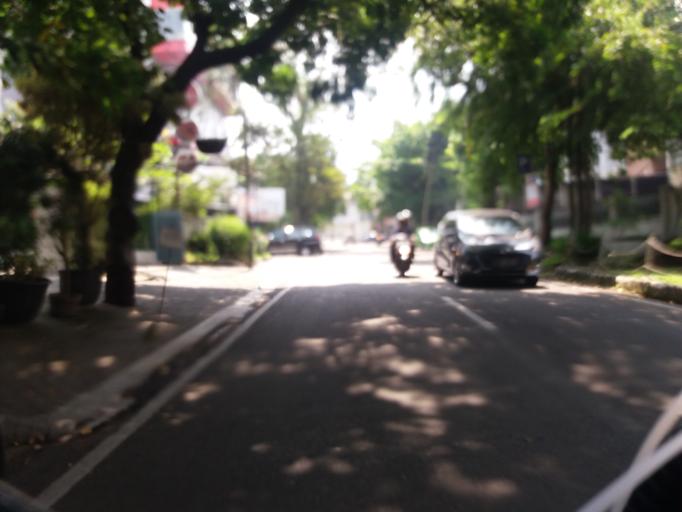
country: ID
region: West Java
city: Bandung
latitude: -6.9013
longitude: 107.6134
